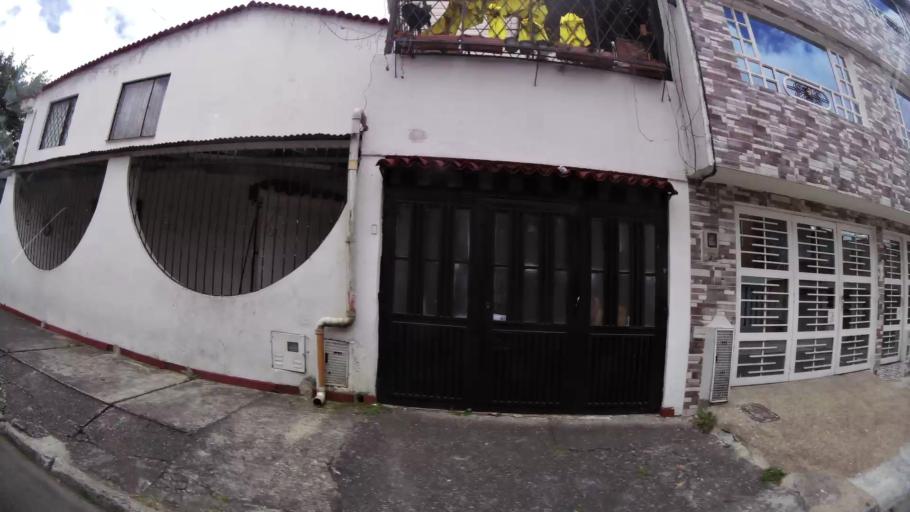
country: CO
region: Bogota D.C.
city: Bogota
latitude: 4.6072
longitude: -74.1100
